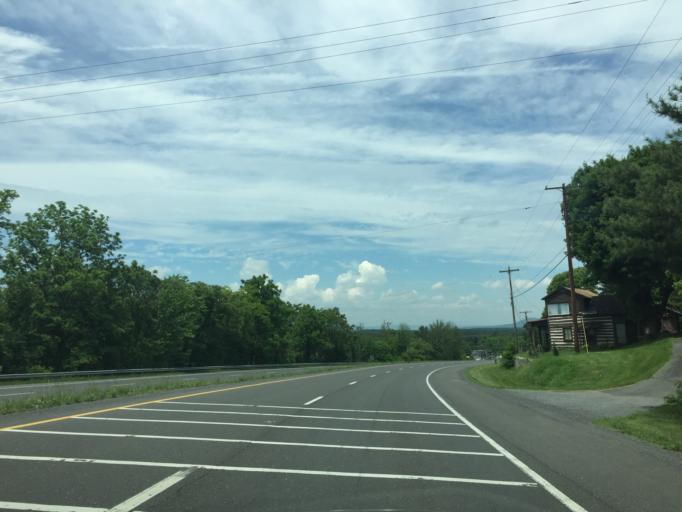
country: US
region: Virginia
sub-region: City of Winchester
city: Winchester
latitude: 39.2408
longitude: -78.2010
